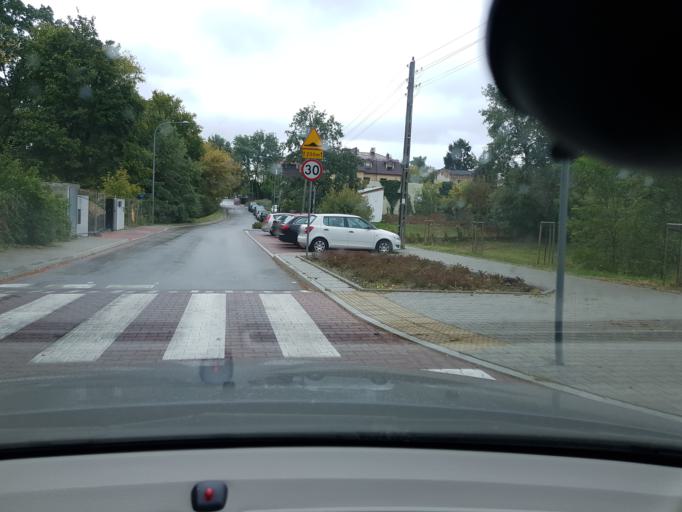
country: PL
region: Masovian Voivodeship
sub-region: Warszawa
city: Zoliborz
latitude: 52.2782
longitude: 20.9656
